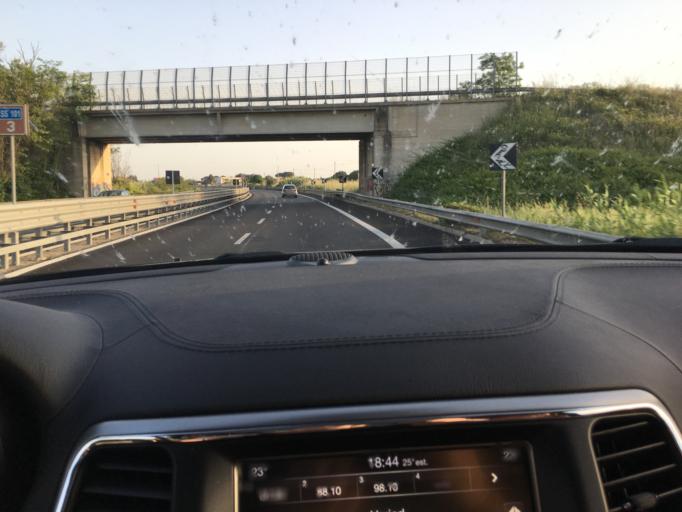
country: IT
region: Apulia
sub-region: Provincia di Lecce
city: San Pietro in Lama
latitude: 40.2994
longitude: 18.1323
